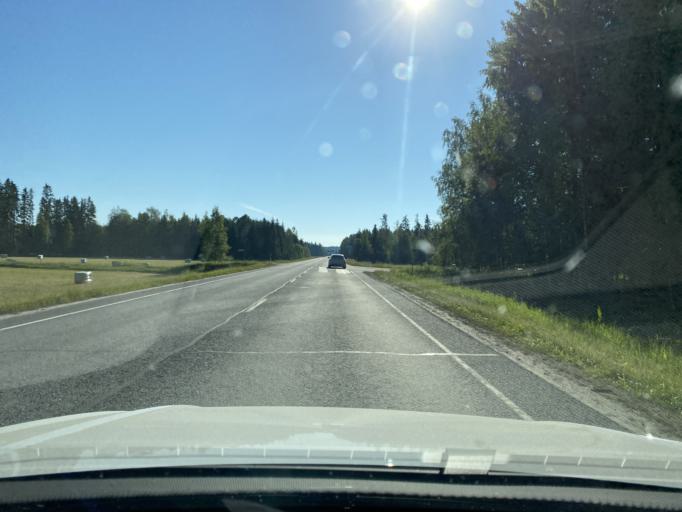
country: FI
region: Haeme
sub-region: Forssa
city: Tammela
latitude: 60.8264
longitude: 23.8023
